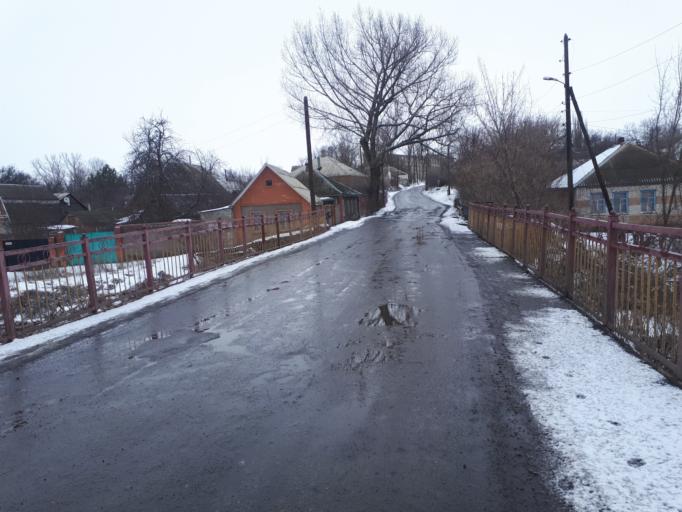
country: RU
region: Rostov
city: Krasnyy Sulin
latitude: 47.8995
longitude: 40.0486
